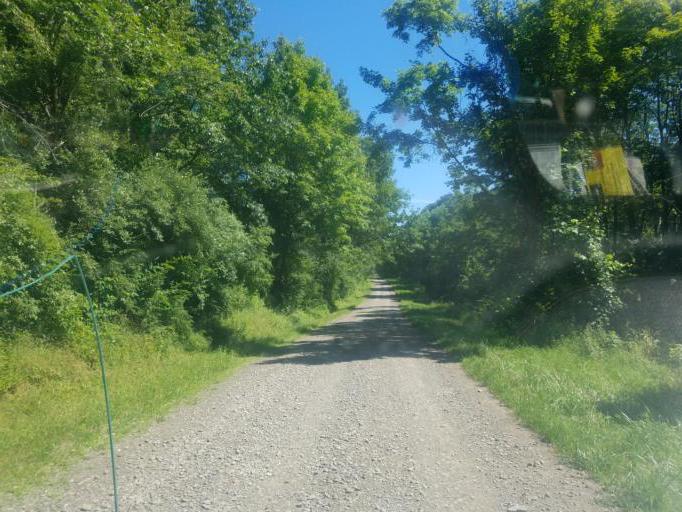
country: US
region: New York
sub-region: Ontario County
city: Naples
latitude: 42.6757
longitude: -77.3363
